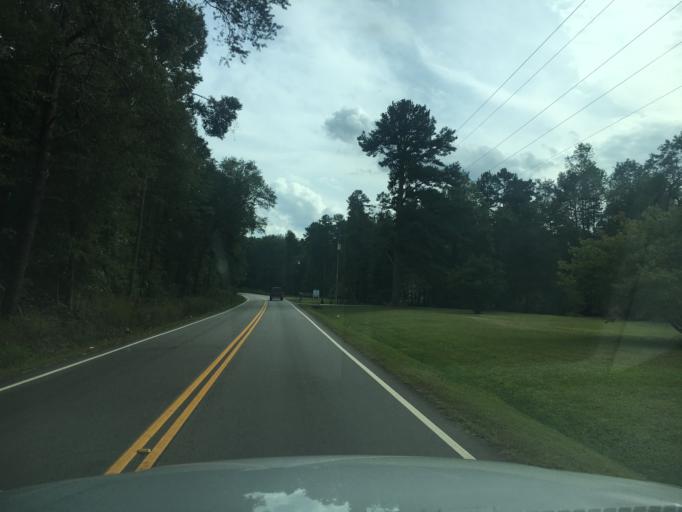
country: US
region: South Carolina
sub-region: Spartanburg County
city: Wellford
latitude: 34.9244
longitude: -82.0627
